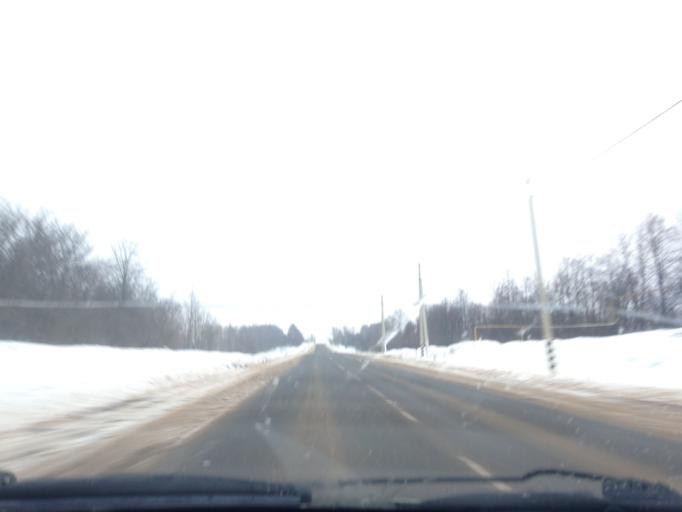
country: RU
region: Tula
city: Shchekino
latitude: 53.9724
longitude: 37.4987
